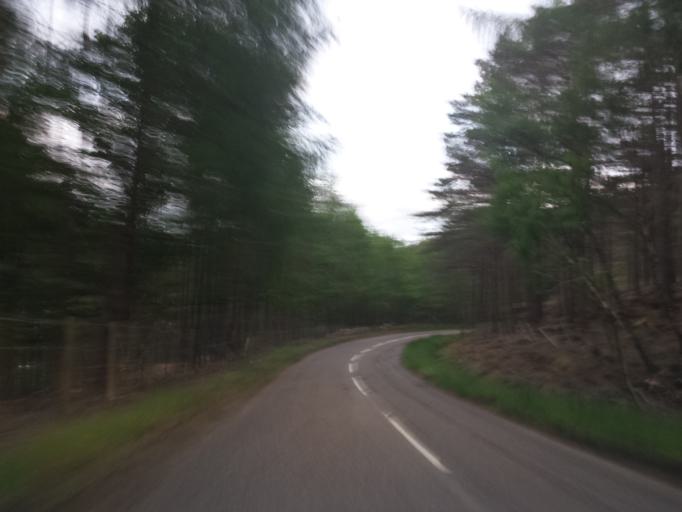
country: GB
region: Scotland
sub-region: Highland
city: Ullapool
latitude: 57.5280
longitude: -5.5329
